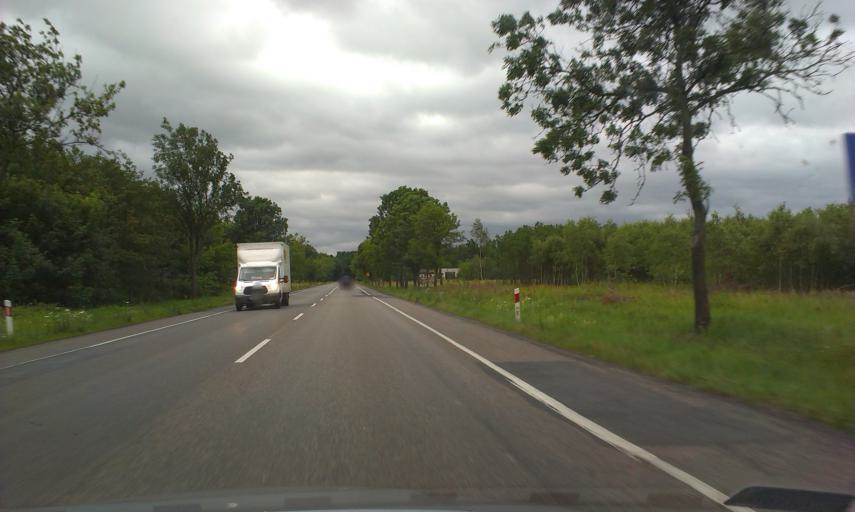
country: PL
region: Greater Poland Voivodeship
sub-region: Powiat obornicki
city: Rogozno
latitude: 52.7290
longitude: 16.9386
